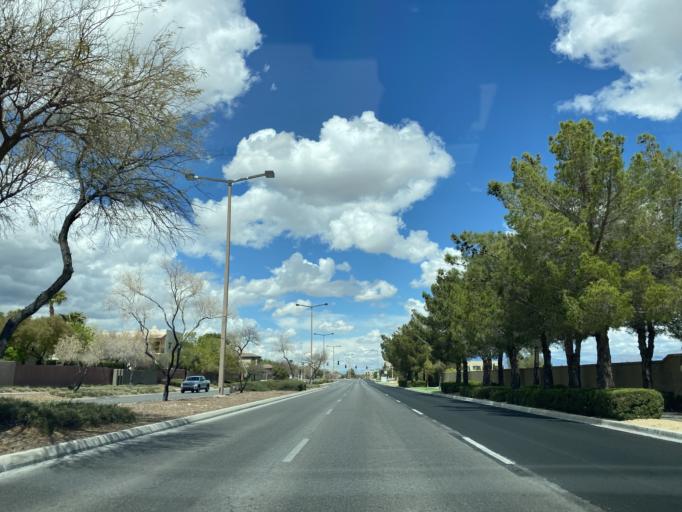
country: US
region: Nevada
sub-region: Clark County
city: Summerlin South
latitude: 36.1657
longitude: -115.3148
